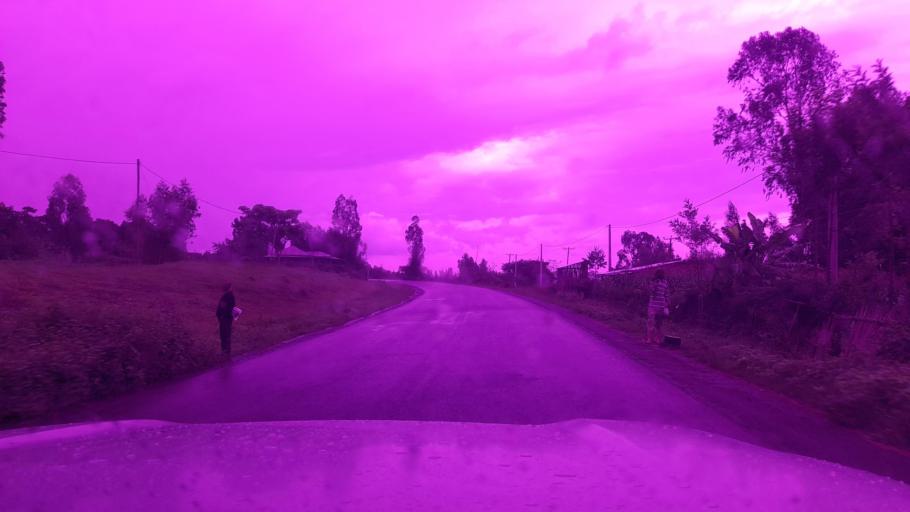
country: ET
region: Oromiya
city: Jima
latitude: 7.7063
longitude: 37.0693
